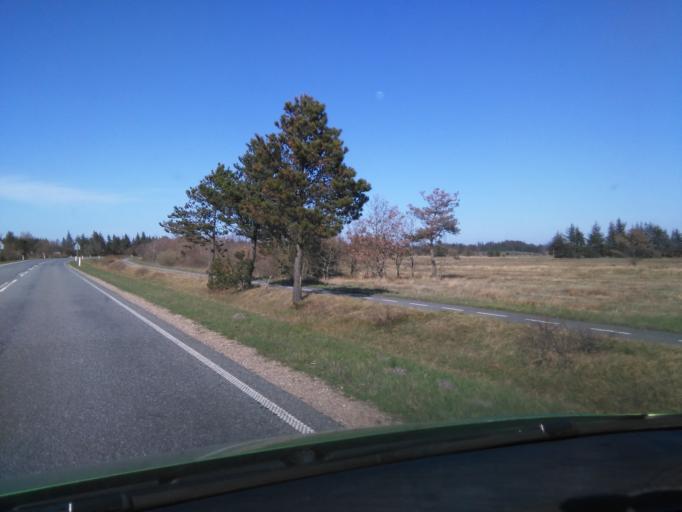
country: DK
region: South Denmark
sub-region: Varde Kommune
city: Oksbol
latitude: 55.6094
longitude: 8.2280
